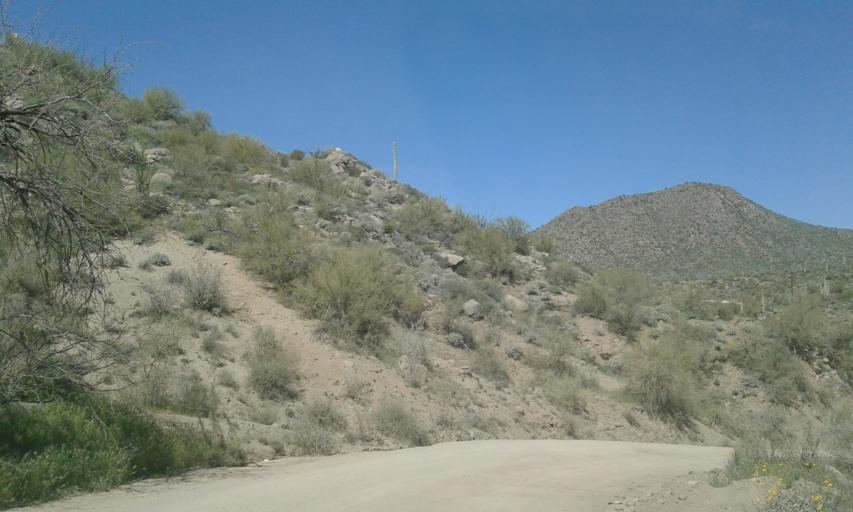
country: US
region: Arizona
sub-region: Gila County
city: Tonto Basin
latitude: 33.5973
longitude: -111.2032
